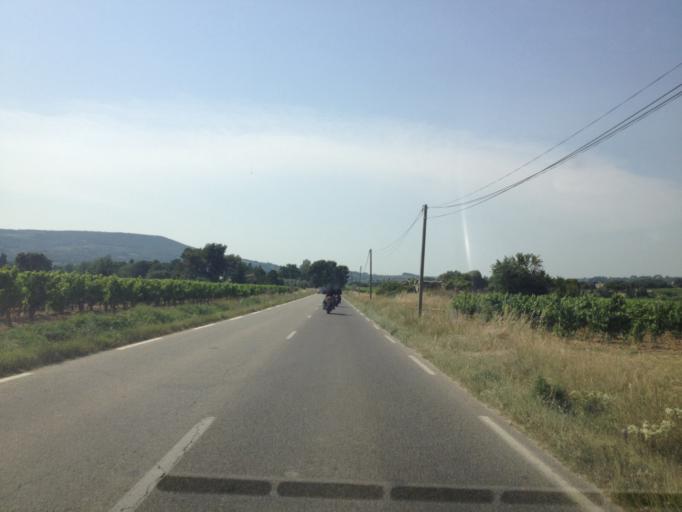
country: FR
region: Provence-Alpes-Cote d'Azur
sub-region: Departement du Vaucluse
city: Vaison-la-Romaine
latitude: 44.2476
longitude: 5.0460
